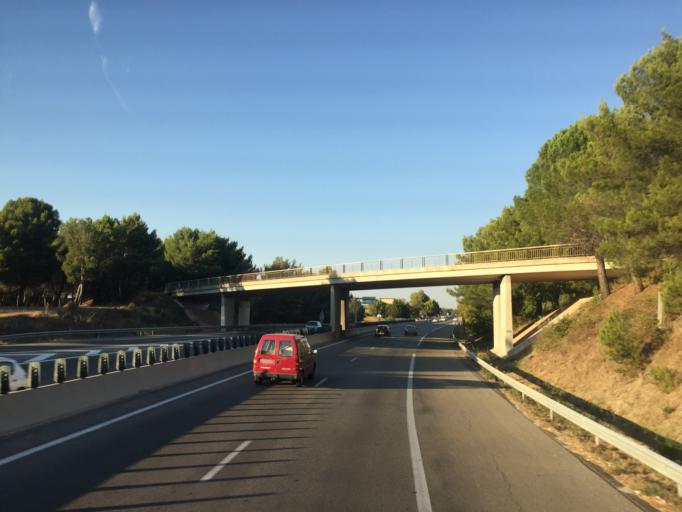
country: FR
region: Provence-Alpes-Cote d'Azur
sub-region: Departement des Bouches-du-Rhone
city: Venelles
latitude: 43.5724
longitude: 5.4683
